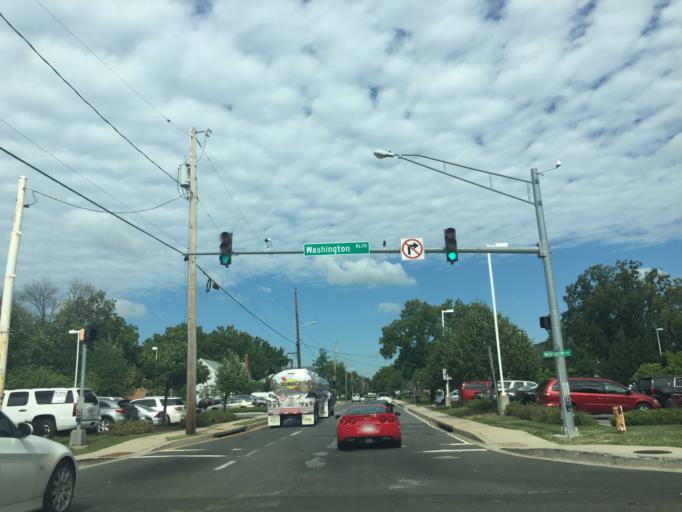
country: US
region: Maryland
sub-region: Prince George's County
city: Laurel
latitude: 39.0994
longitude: -76.8482
